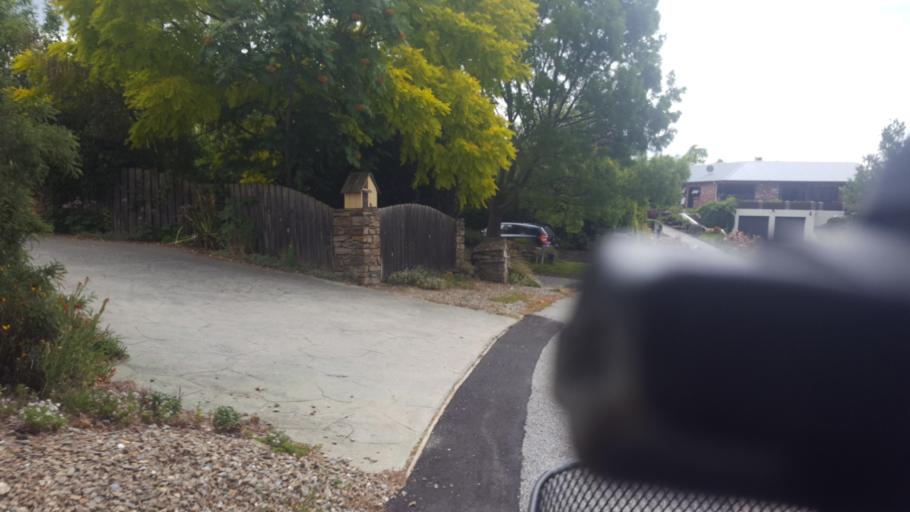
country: NZ
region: Otago
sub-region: Queenstown-Lakes District
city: Wanaka
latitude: -45.2609
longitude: 169.3816
